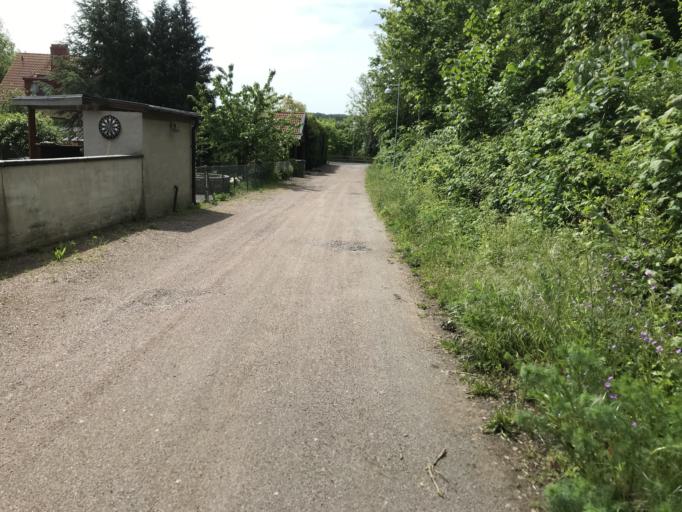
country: SE
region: Skane
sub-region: Landskrona
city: Landskrona
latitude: 55.9007
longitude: 12.8315
